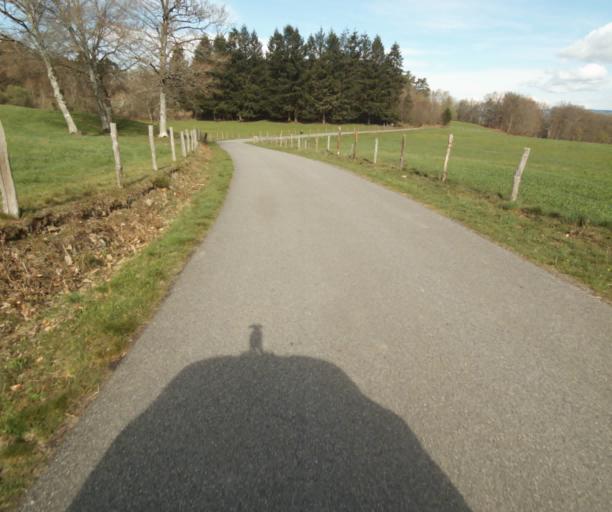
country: FR
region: Limousin
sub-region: Departement de la Correze
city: Correze
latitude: 45.3344
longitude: 1.8569
